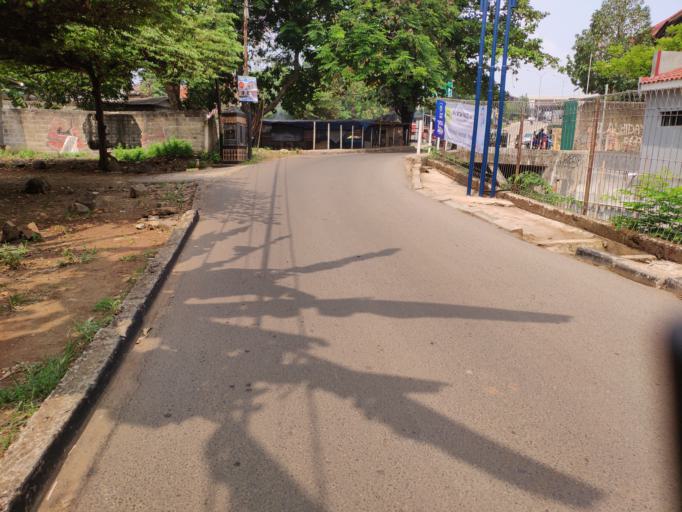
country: ID
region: West Java
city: Pamulang
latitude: -6.3252
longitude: 106.8044
